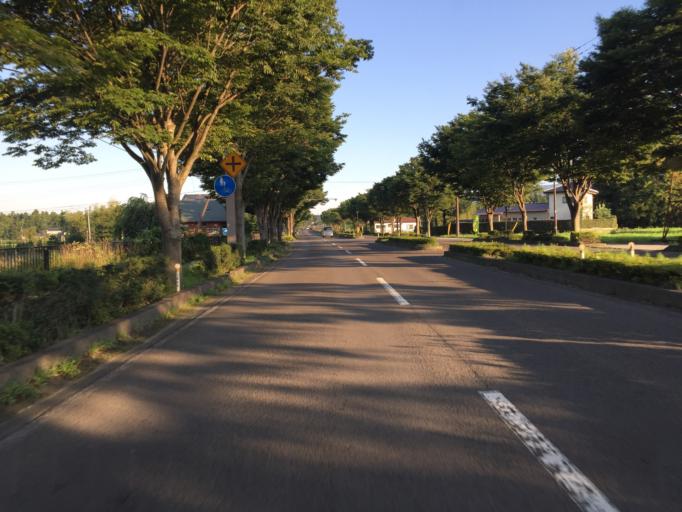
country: JP
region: Fukushima
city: Fukushima-shi
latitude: 37.7403
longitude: 140.3831
